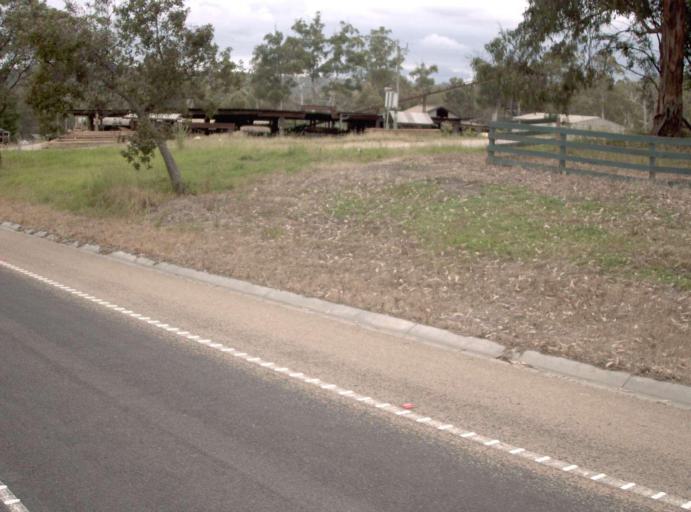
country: AU
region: Victoria
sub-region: East Gippsland
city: Lakes Entrance
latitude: -37.7267
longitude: 148.0884
